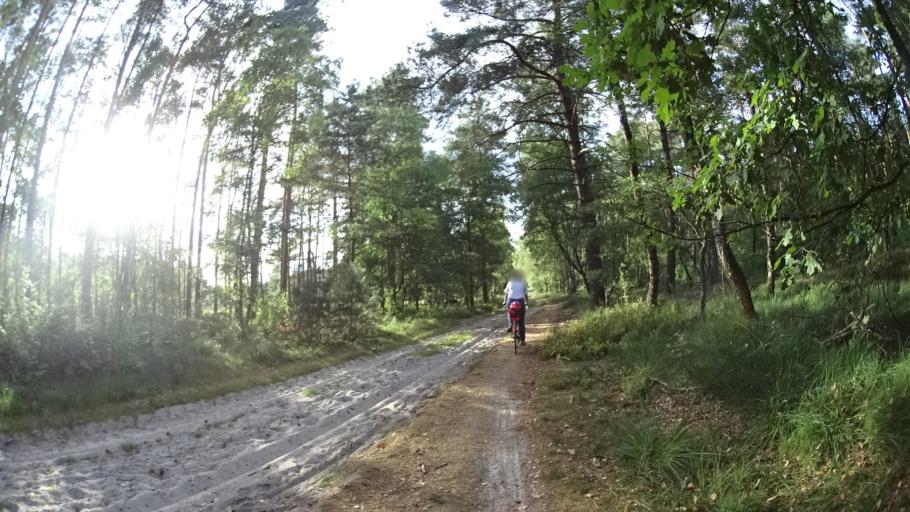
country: DE
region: Lower Saxony
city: Handeloh
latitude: 53.2225
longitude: 9.8770
